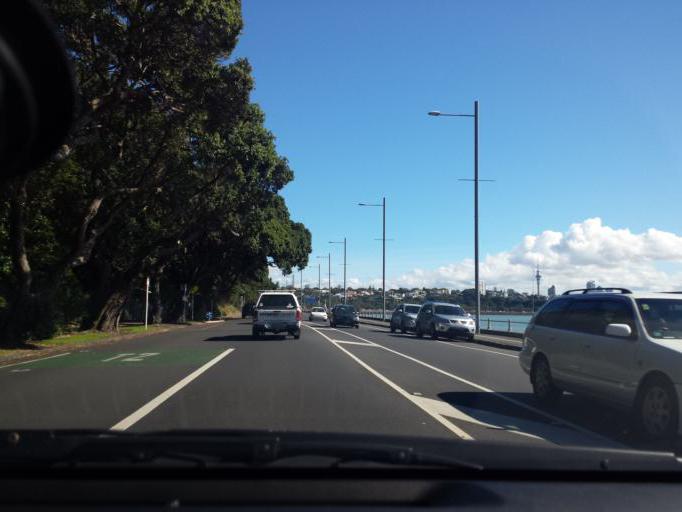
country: NZ
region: Auckland
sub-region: Auckland
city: Auckland
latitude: -36.8520
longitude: 174.8077
